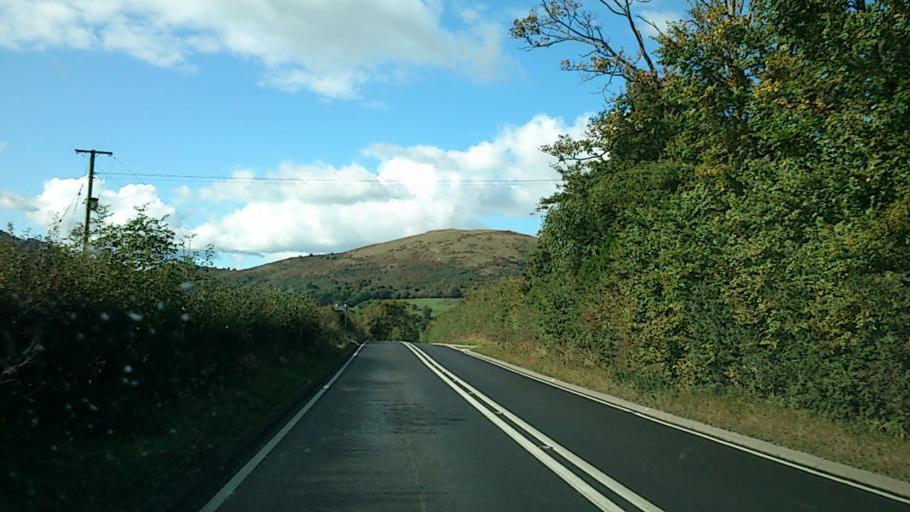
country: GB
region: England
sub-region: Shropshire
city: Westbury
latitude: 52.7056
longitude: -3.0080
